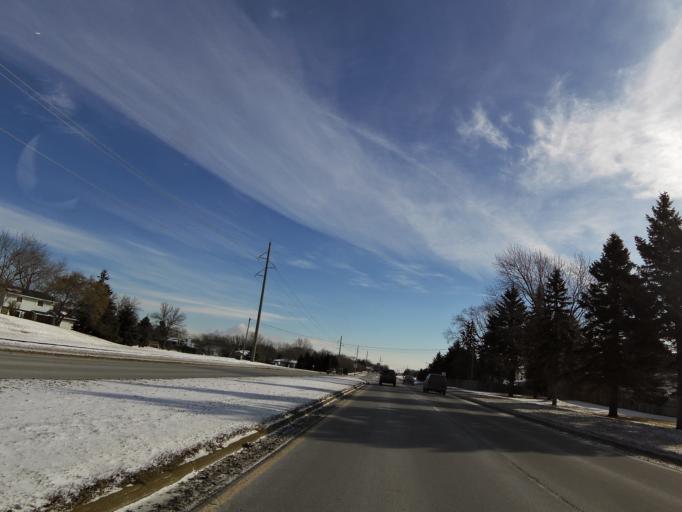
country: US
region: Minnesota
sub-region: Dakota County
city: Rosemount
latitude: 44.7318
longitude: -93.1644
